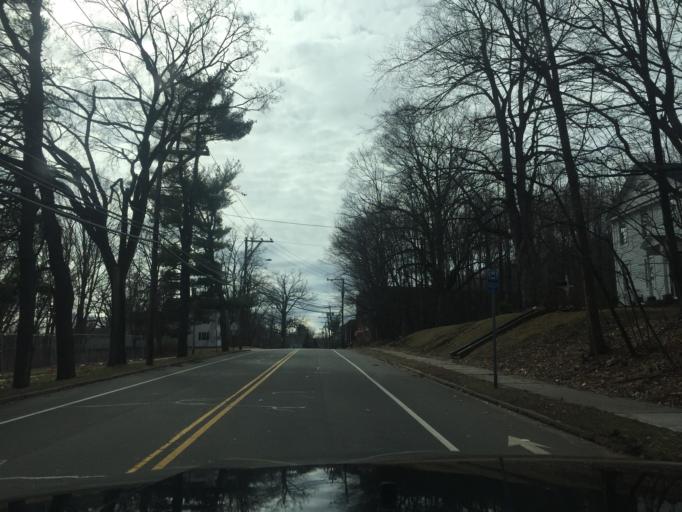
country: US
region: Connecticut
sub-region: Hartford County
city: New Britain
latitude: 41.7041
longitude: -72.7757
